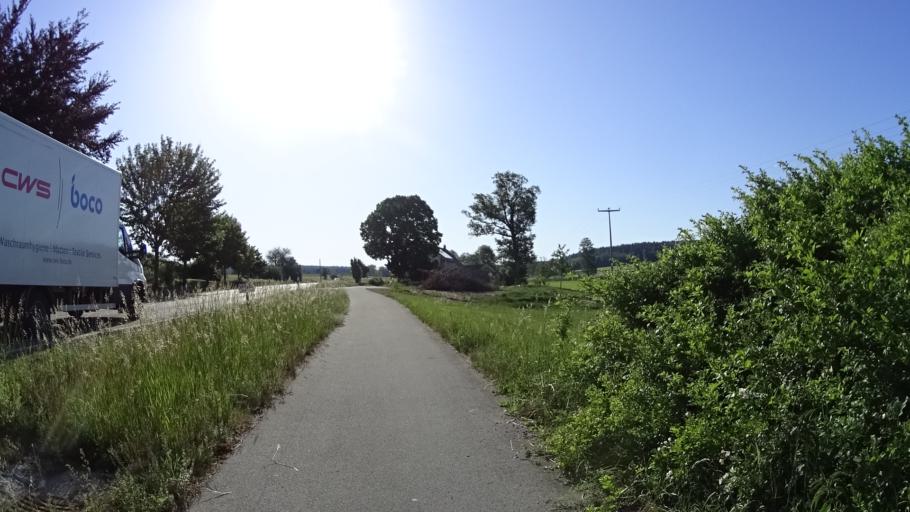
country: DE
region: Bavaria
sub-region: Regierungsbezirk Mittelfranken
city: Wieseth
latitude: 49.1611
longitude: 10.4906
